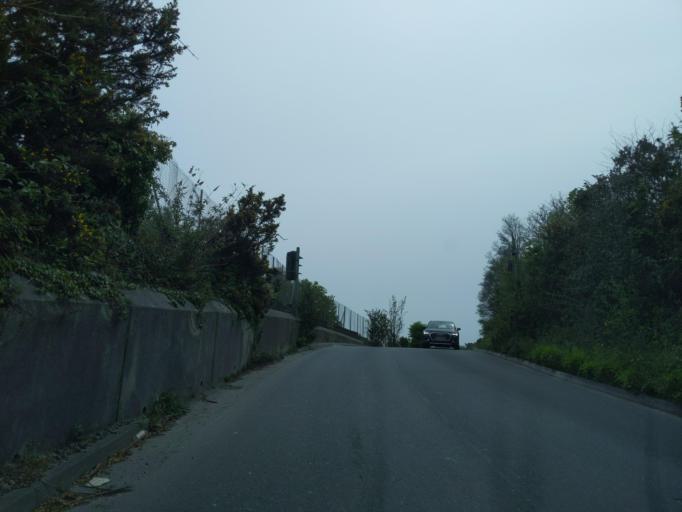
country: GB
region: England
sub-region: Cornwall
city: Par
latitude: 50.3459
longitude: -4.7074
